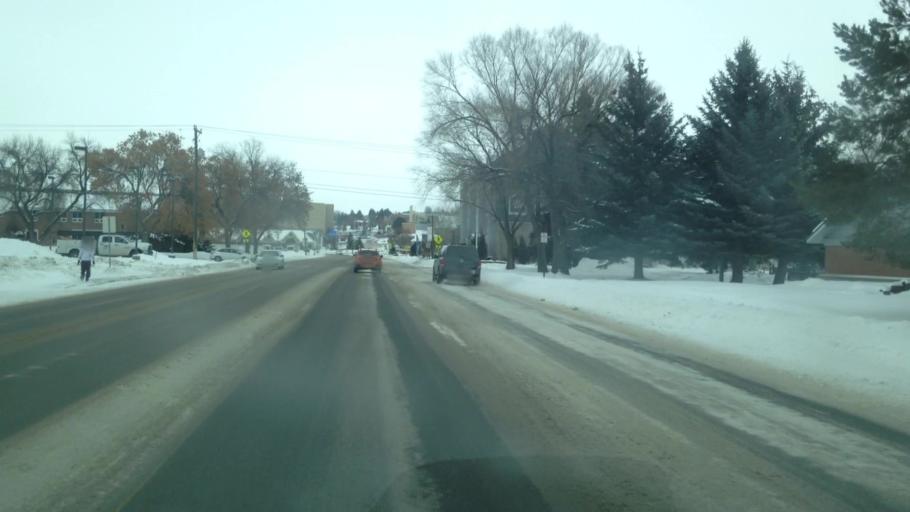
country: US
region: Idaho
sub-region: Madison County
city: Rexburg
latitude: 43.8177
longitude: -111.7936
